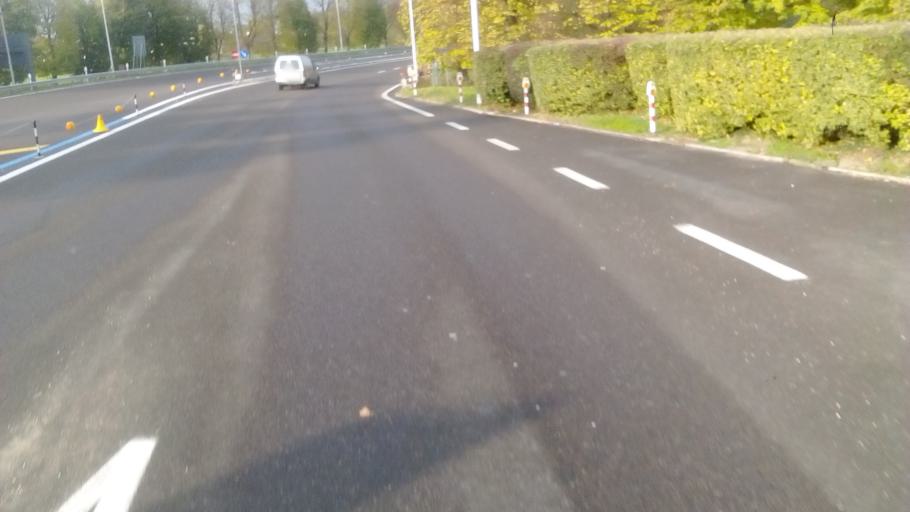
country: IT
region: Veneto
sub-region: Provincia di Vicenza
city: Dueville
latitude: 45.6387
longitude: 11.5661
